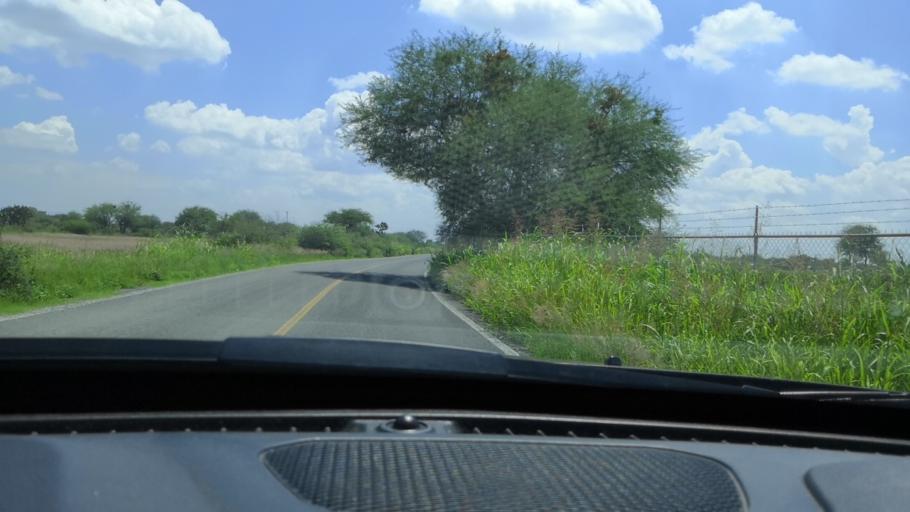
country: MX
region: Guanajuato
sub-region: Leon
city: Plan Guanajuato (La Sandia)
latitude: 20.9503
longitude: -101.6050
